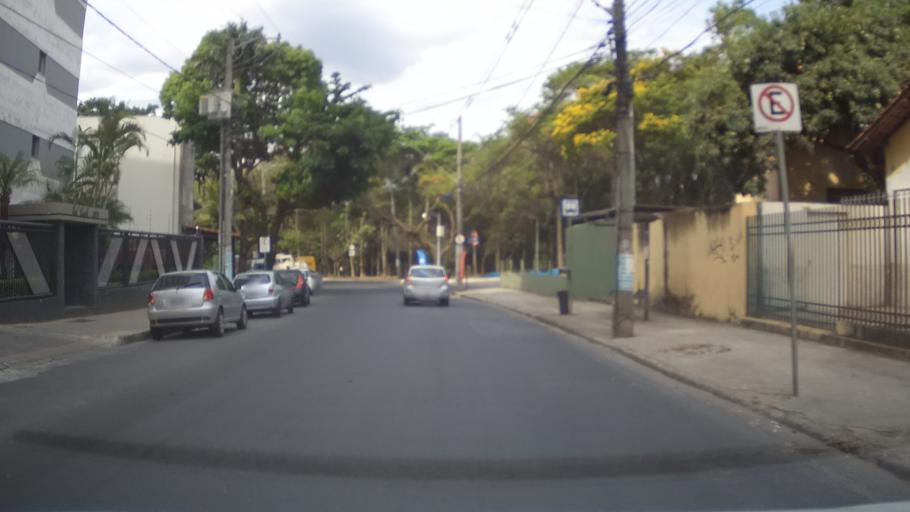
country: BR
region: Minas Gerais
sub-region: Belo Horizonte
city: Belo Horizonte
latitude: -19.8947
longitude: -43.9219
